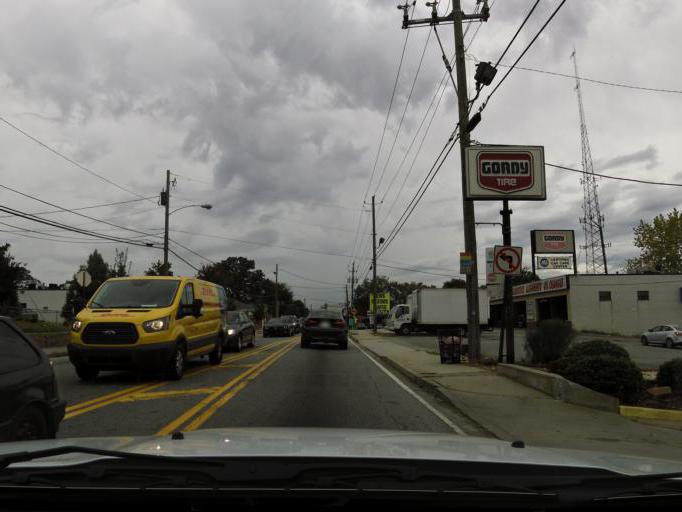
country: US
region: Georgia
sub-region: Fulton County
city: Atlanta
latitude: 33.7990
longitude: -84.4161
